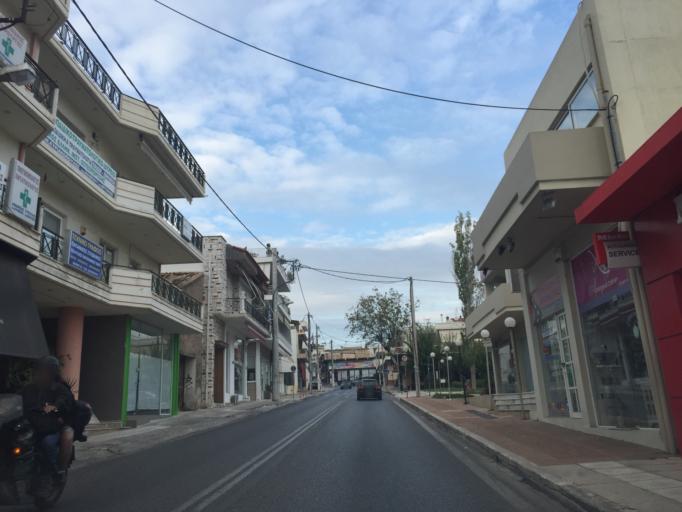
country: GR
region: Attica
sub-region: Nomarchia Anatolikis Attikis
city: Vari
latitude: 37.8316
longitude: 23.8026
